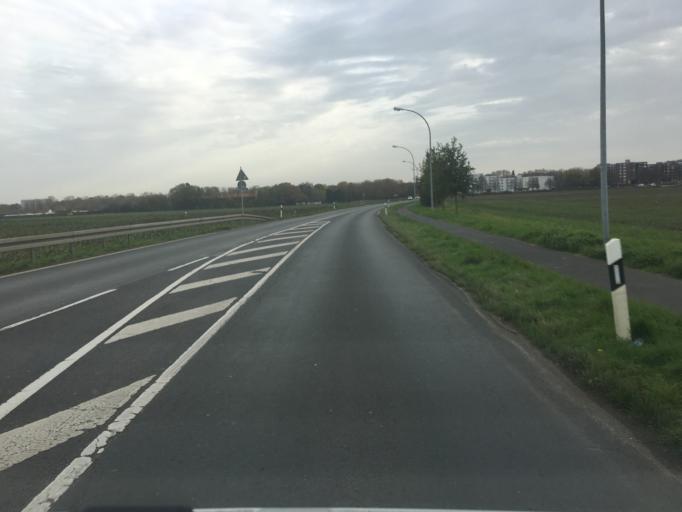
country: DE
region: North Rhine-Westphalia
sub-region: Regierungsbezirk Koln
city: Hurth
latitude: 50.8911
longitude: 6.8742
